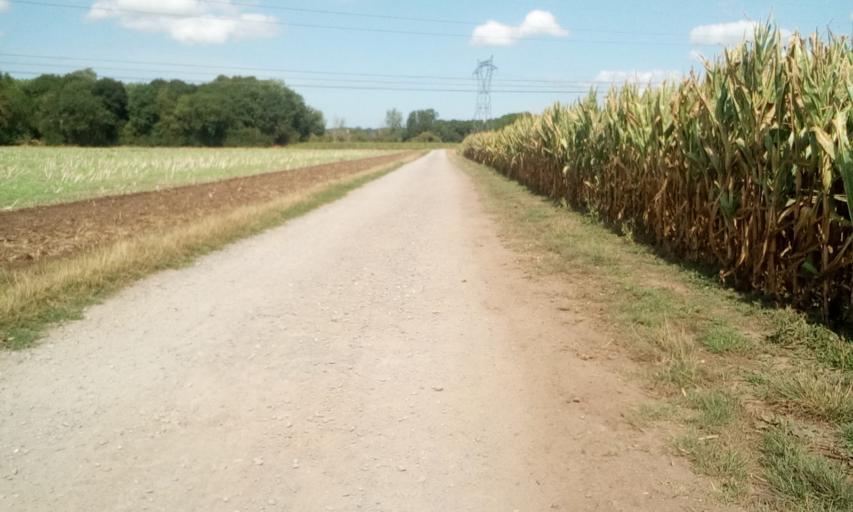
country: FR
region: Lower Normandy
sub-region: Departement du Calvados
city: Argences
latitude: 49.1331
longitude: -0.1826
